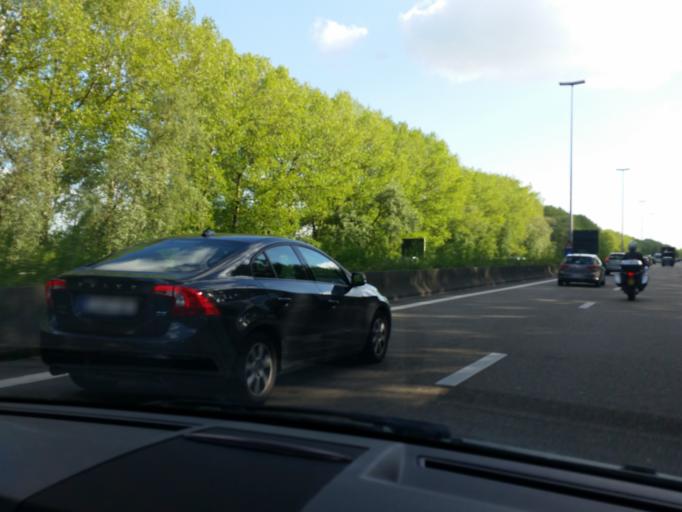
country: BE
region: Flanders
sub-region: Provincie Oost-Vlaanderen
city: Waasmunster
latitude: 51.1138
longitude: 4.0600
